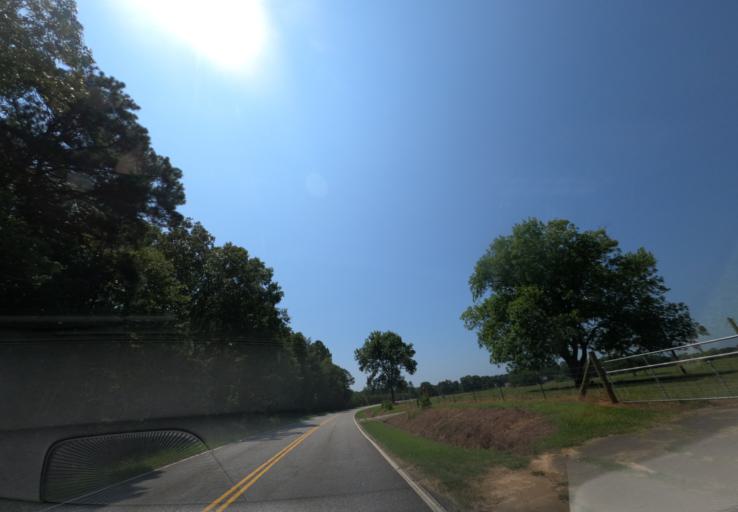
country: US
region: South Carolina
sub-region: Greenwood County
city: Greenwood
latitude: 34.0120
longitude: -82.1245
